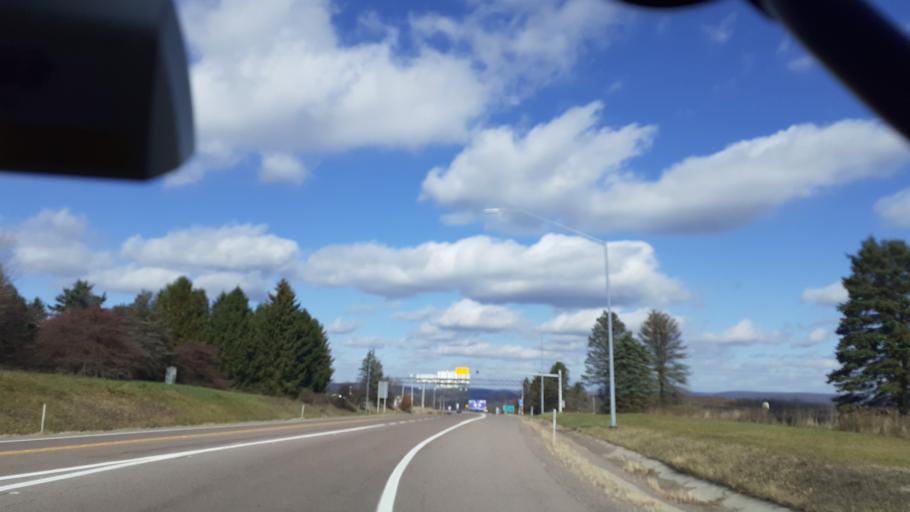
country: US
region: Pennsylvania
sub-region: Somerset County
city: Meyersdale
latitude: 39.6920
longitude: -79.2484
